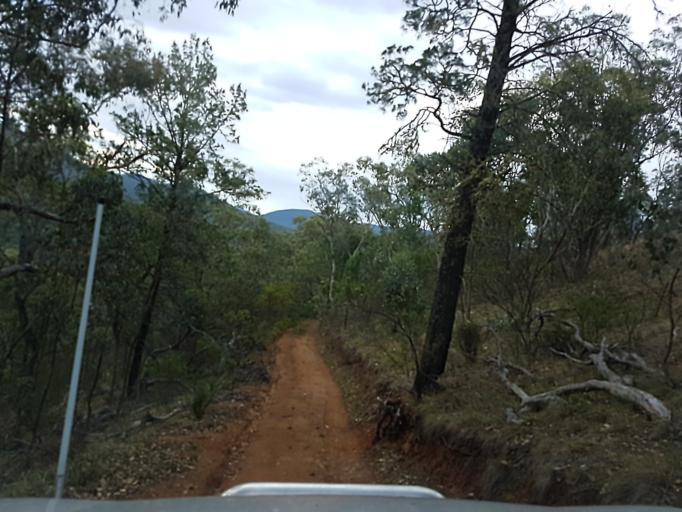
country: AU
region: New South Wales
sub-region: Snowy River
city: Jindabyne
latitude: -36.9549
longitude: 148.3820
